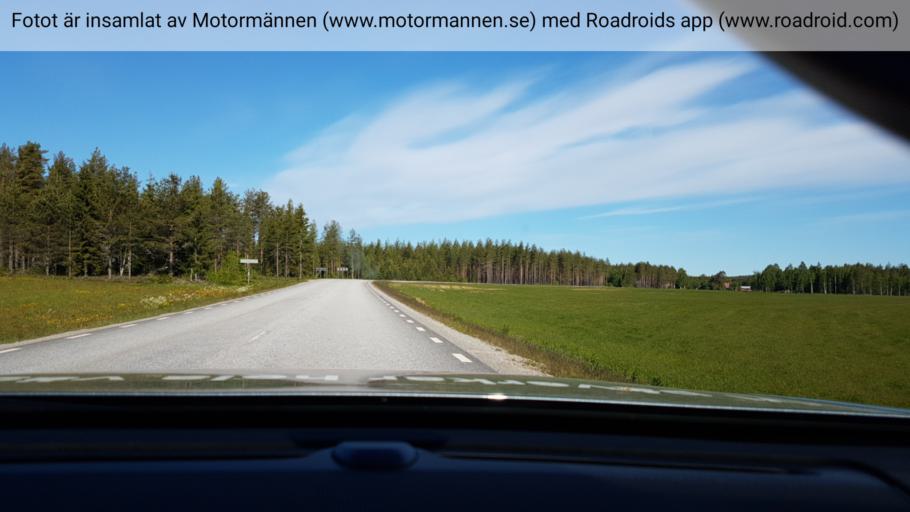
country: SE
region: Vaesterbotten
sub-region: Vindelns Kommun
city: Vindeln
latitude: 64.1139
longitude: 19.5744
